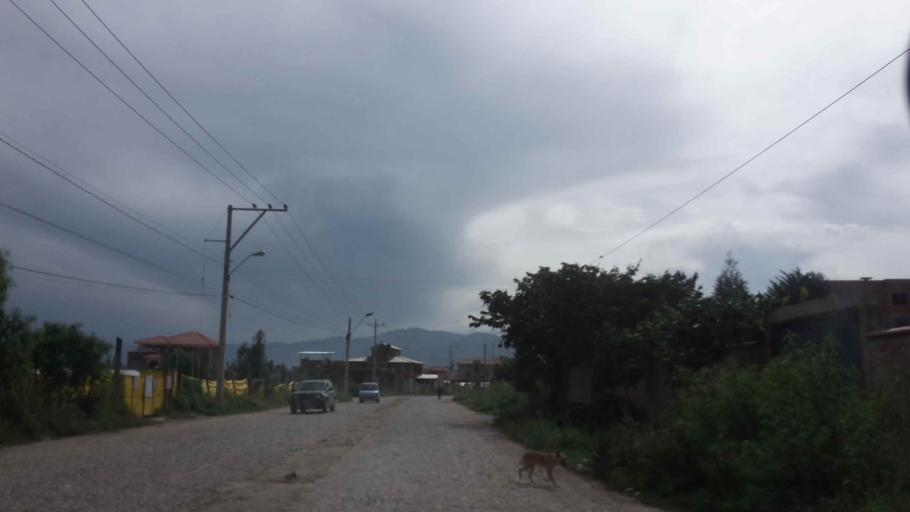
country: BO
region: Cochabamba
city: Cochabamba
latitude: -17.3359
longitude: -66.2573
